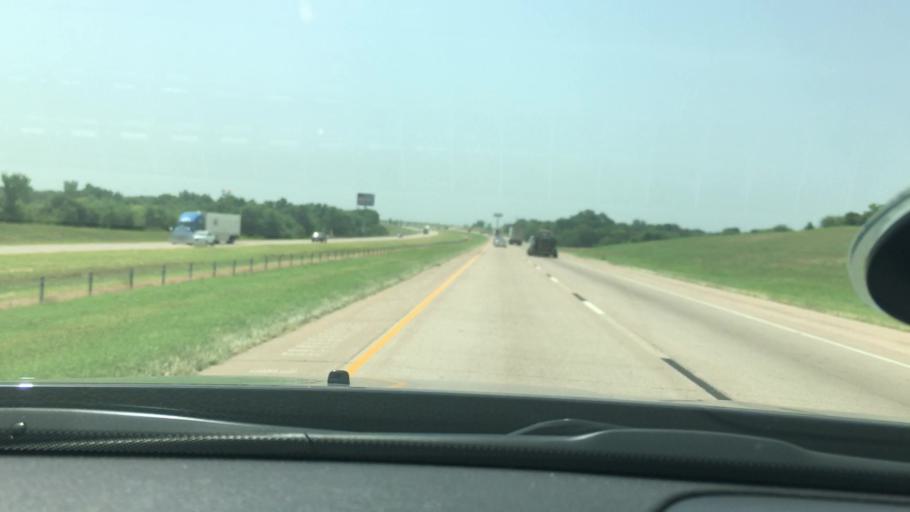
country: US
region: Oklahoma
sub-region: Garvin County
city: Pauls Valley
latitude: 34.7186
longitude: -97.2518
